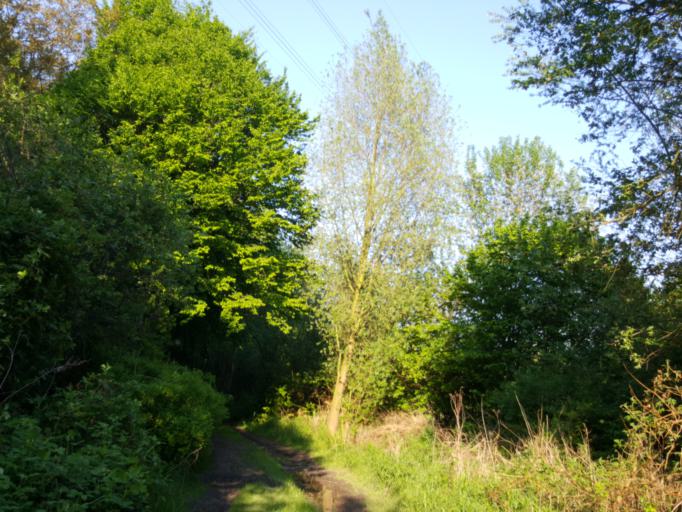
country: DE
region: Schleswig-Holstein
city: Oststeinbek
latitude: 53.5188
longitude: 10.1665
